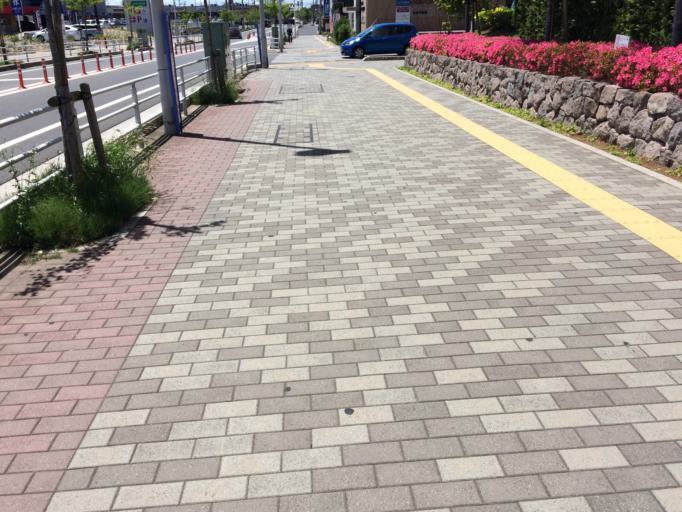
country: JP
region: Saitama
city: Yoshikawa
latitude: 35.8674
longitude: 139.8575
